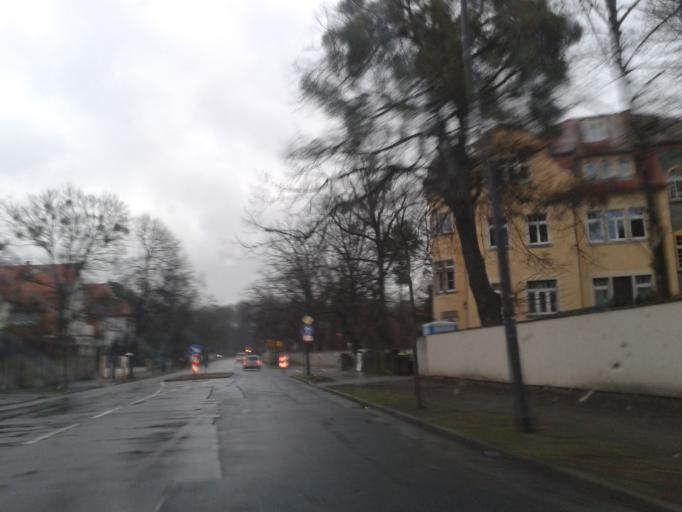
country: DE
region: Saxony
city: Albertstadt
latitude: 51.0695
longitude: 13.7831
